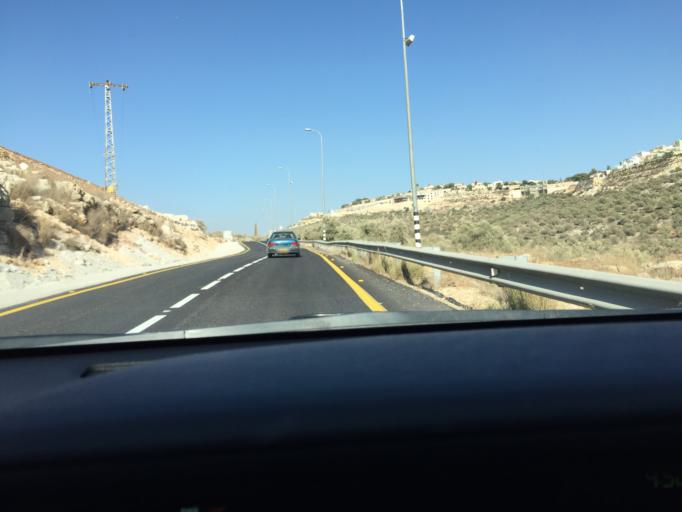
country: PS
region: West Bank
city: Rafat
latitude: 32.0642
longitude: 35.0440
